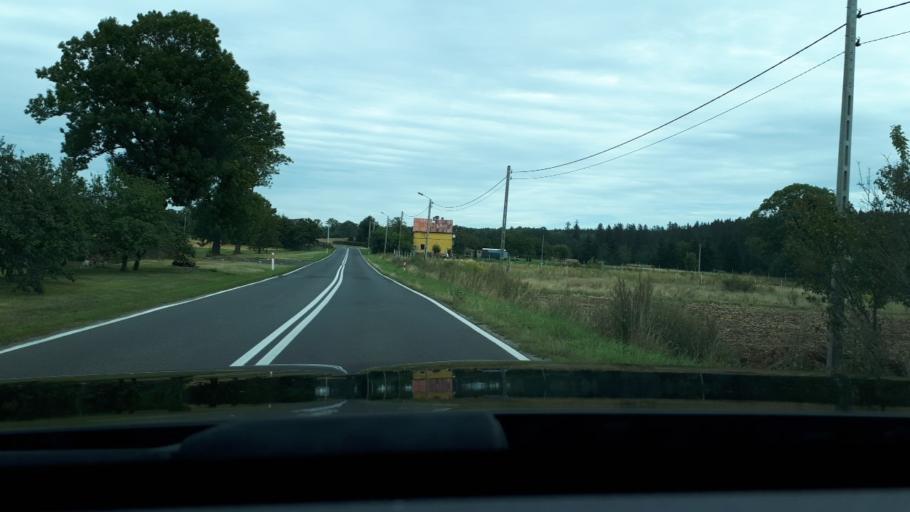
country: PL
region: Lower Silesian Voivodeship
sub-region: Powiat lwowecki
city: Gryfow Slaski
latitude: 51.0477
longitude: 15.4509
